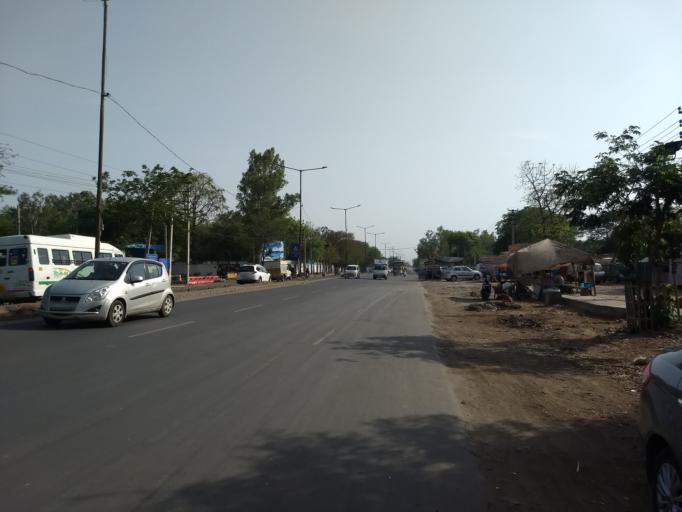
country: IN
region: Haryana
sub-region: Gurgaon
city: Gurgaon
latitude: 28.4853
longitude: 77.0524
